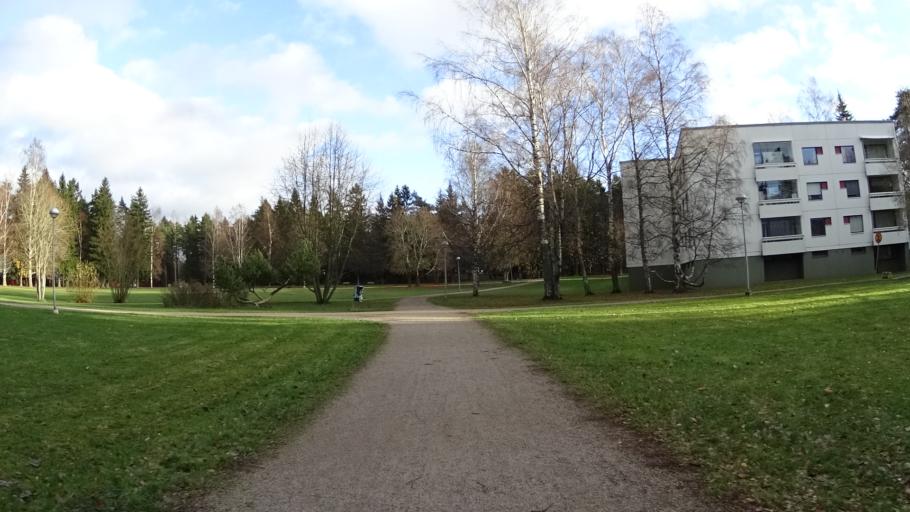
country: FI
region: Uusimaa
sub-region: Helsinki
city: Vantaa
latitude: 60.3057
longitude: 25.0259
